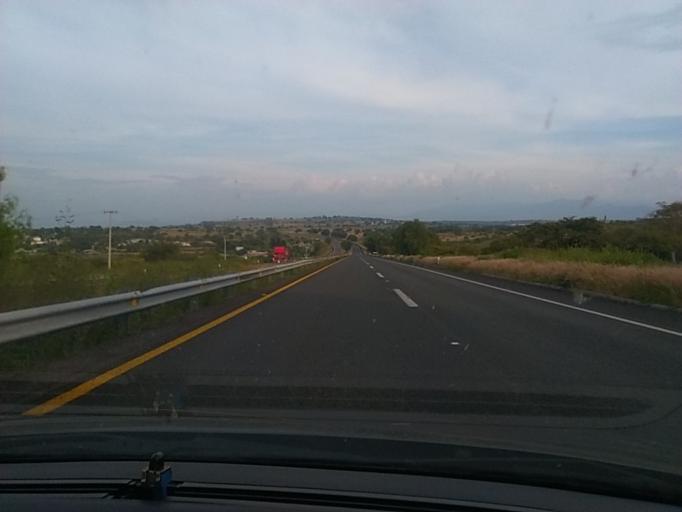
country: MX
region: Michoacan
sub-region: Cuitzeo
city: San Juan Benito Juarez (San Juan Tararameo)
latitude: 19.8958
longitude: -101.0777
